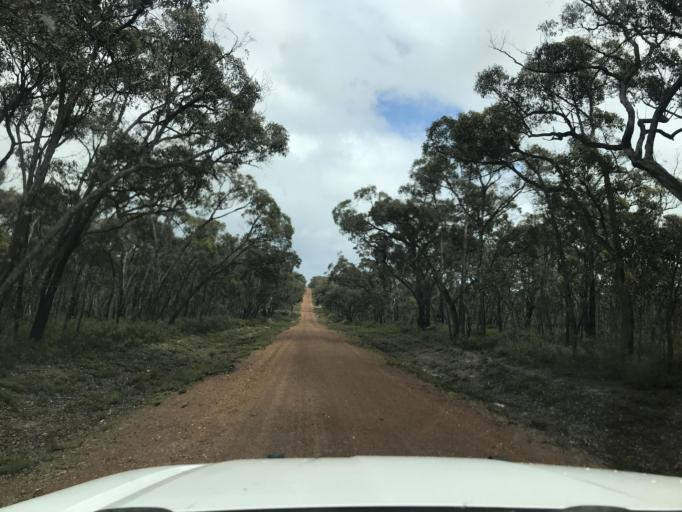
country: AU
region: South Australia
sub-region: Wattle Range
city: Penola
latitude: -37.2950
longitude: 141.3162
